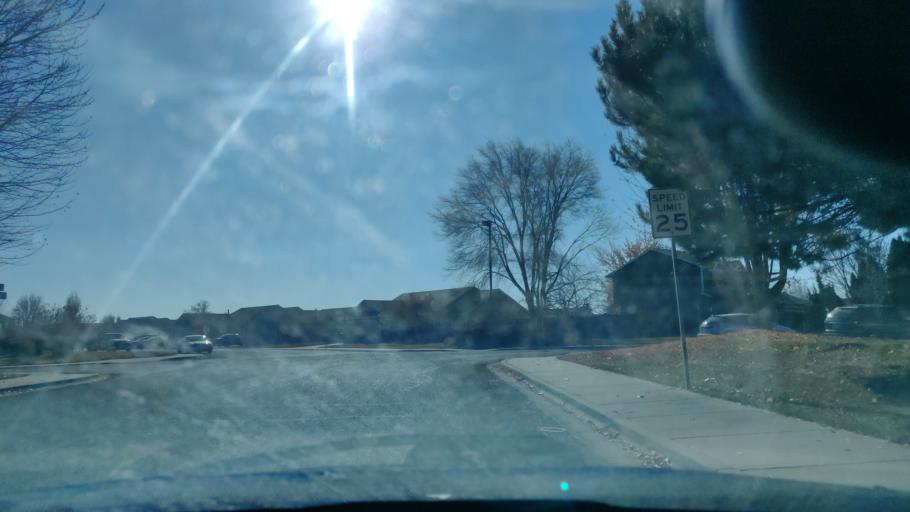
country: US
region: Idaho
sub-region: Ada County
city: Meridian
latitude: 43.6118
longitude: -116.4234
